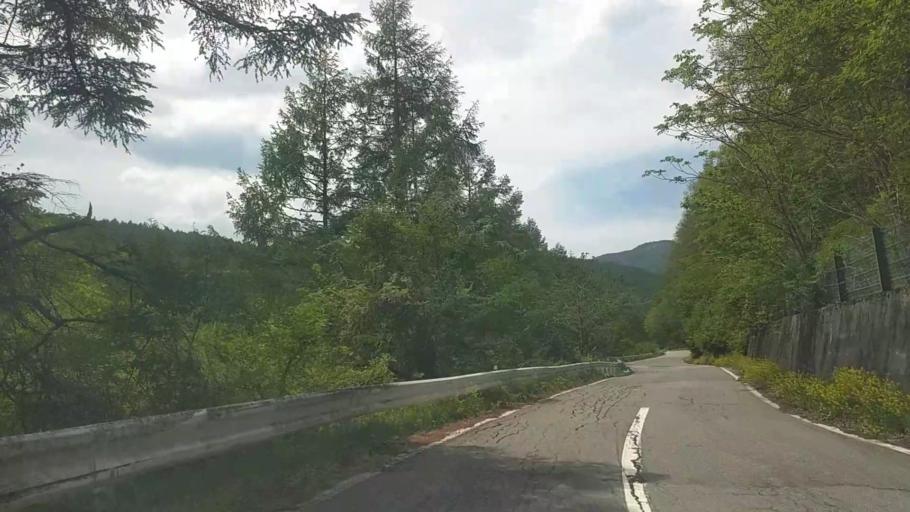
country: JP
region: Nagano
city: Saku
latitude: 36.1008
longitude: 138.3931
